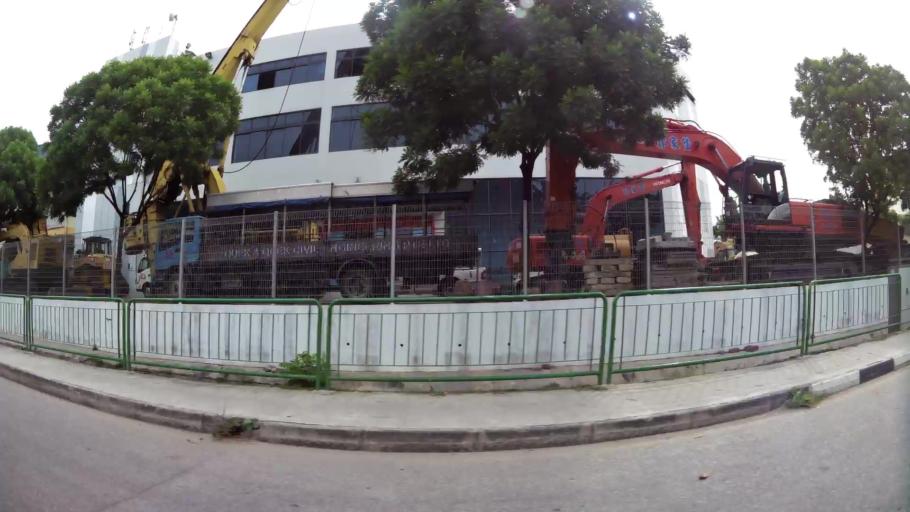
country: MY
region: Johor
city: Johor Bahru
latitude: 1.4367
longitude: 103.7464
